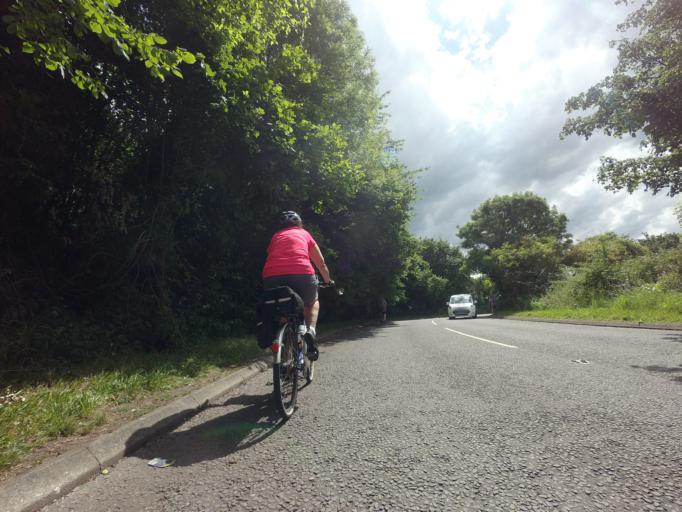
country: GB
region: England
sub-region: Medway
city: Rochester
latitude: 51.4156
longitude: 0.5230
